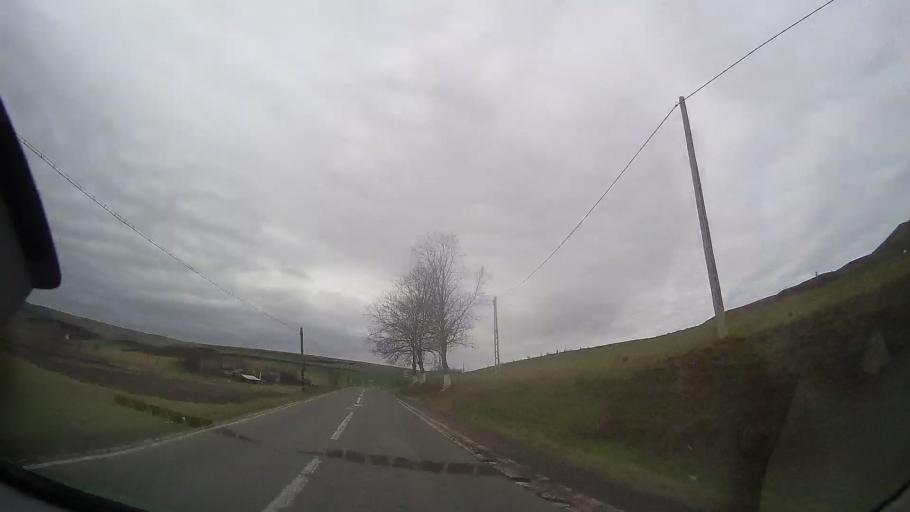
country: RO
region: Bistrita-Nasaud
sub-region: Comuna Urmenis
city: Urmenis
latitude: 46.7610
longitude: 24.3860
